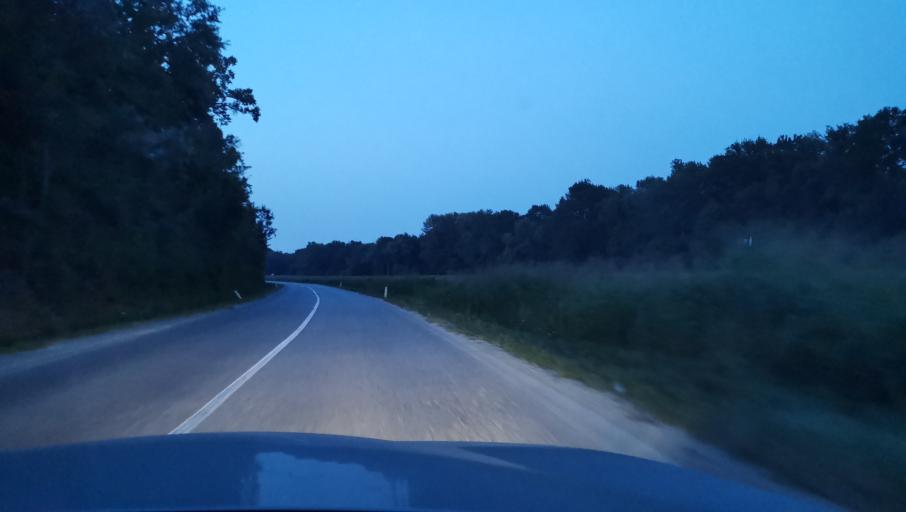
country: RS
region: Central Serbia
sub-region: Belgrade
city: Obrenovac
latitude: 44.6797
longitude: 20.1876
